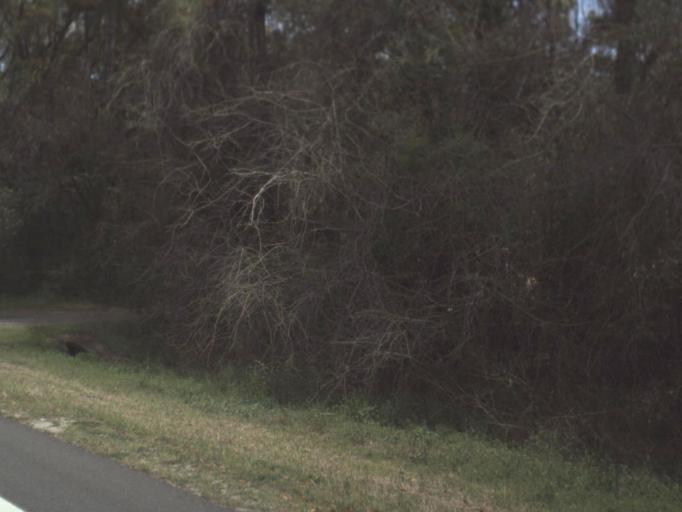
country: US
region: Florida
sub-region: Wakulla County
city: Crawfordville
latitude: 30.2728
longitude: -84.3595
